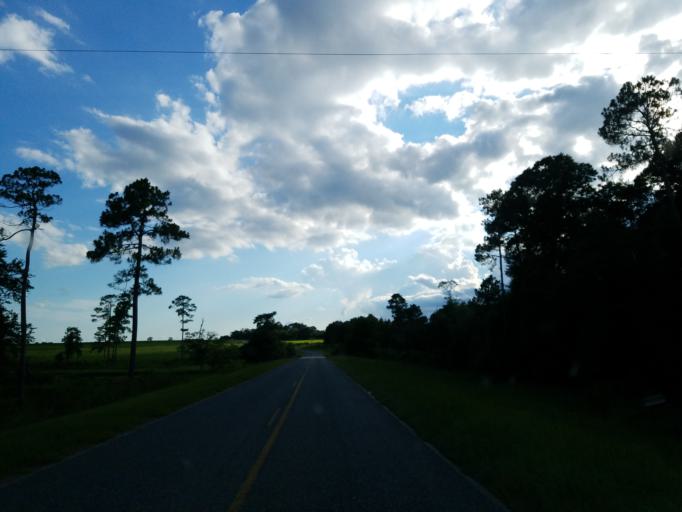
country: US
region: Georgia
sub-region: Turner County
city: Ashburn
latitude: 31.6242
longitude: -83.5846
